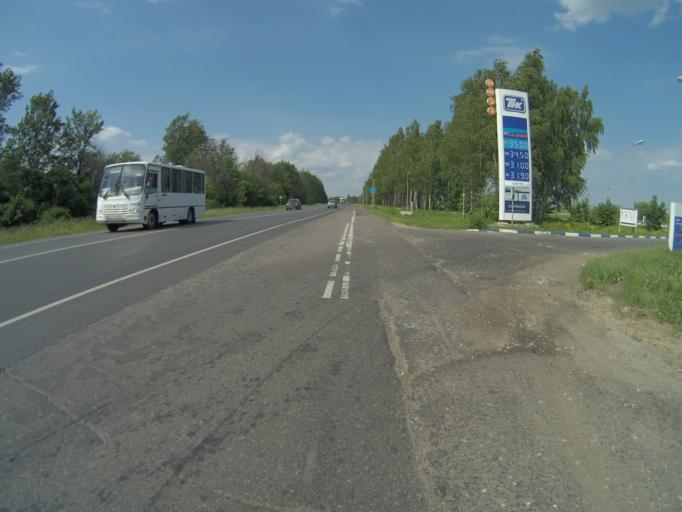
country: RU
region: Vladimir
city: Suzdal'
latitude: 56.3719
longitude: 40.4621
